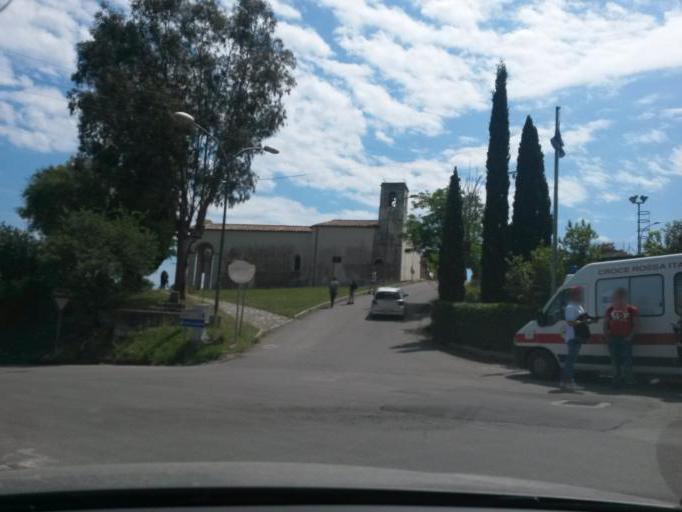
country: IT
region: Tuscany
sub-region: Provincia di Livorno
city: Rio nell'Elba
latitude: 42.8110
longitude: 10.4020
